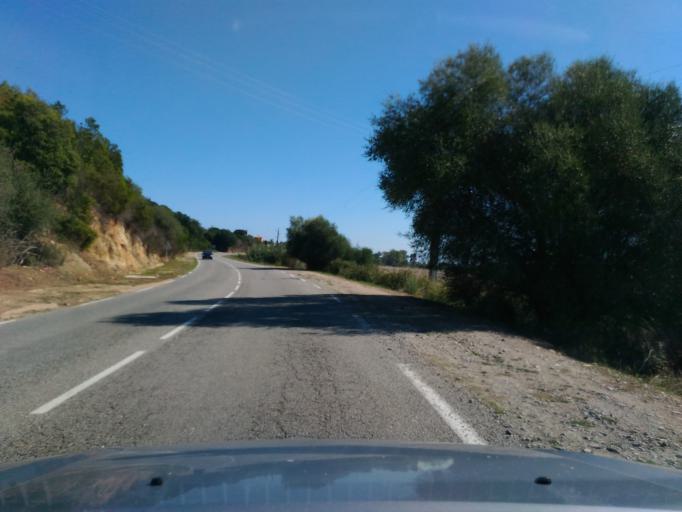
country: FR
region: Corsica
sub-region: Departement de la Haute-Corse
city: Aleria
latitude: 42.1138
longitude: 9.4996
